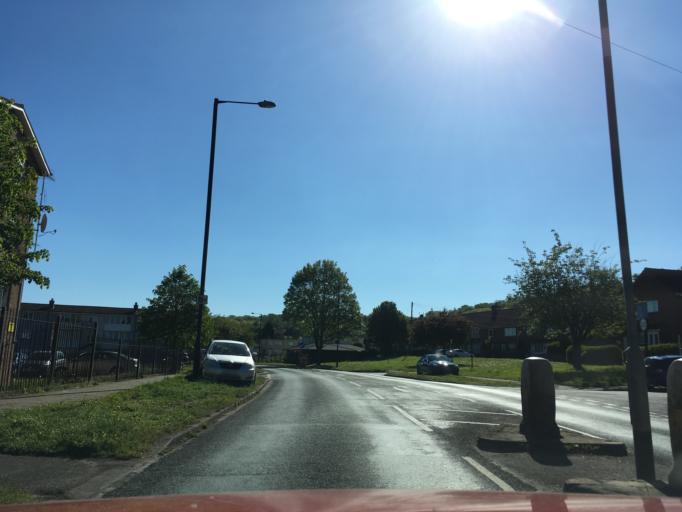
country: GB
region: England
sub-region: North Somerset
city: Easton-in-Gordano
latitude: 51.4950
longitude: -2.6745
